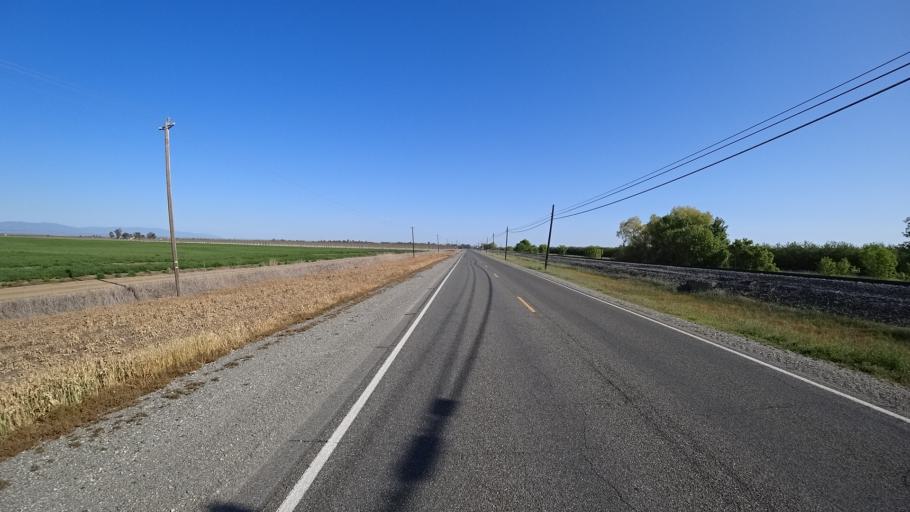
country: US
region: California
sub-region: Glenn County
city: Willows
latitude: 39.5614
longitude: -122.1937
